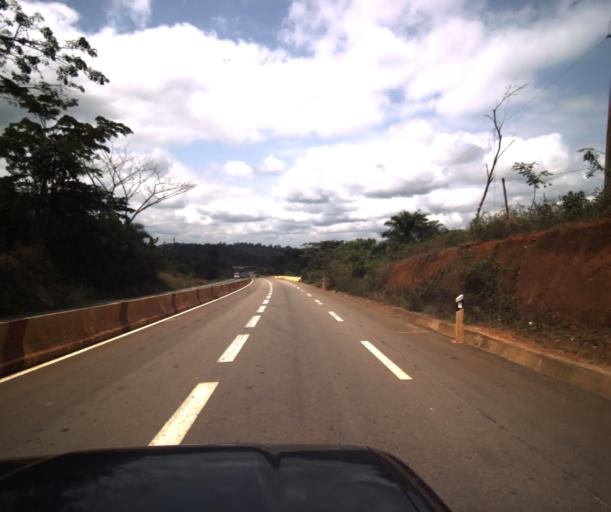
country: CM
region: Centre
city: Mbankomo
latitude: 3.7998
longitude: 11.3355
